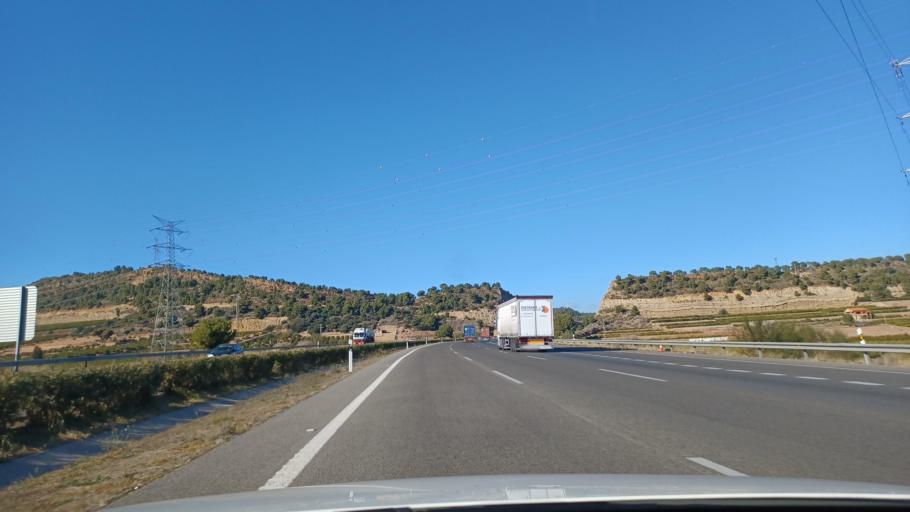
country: ES
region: Valencia
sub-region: Provincia de Valencia
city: Petres
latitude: 39.6540
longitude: -0.3040
